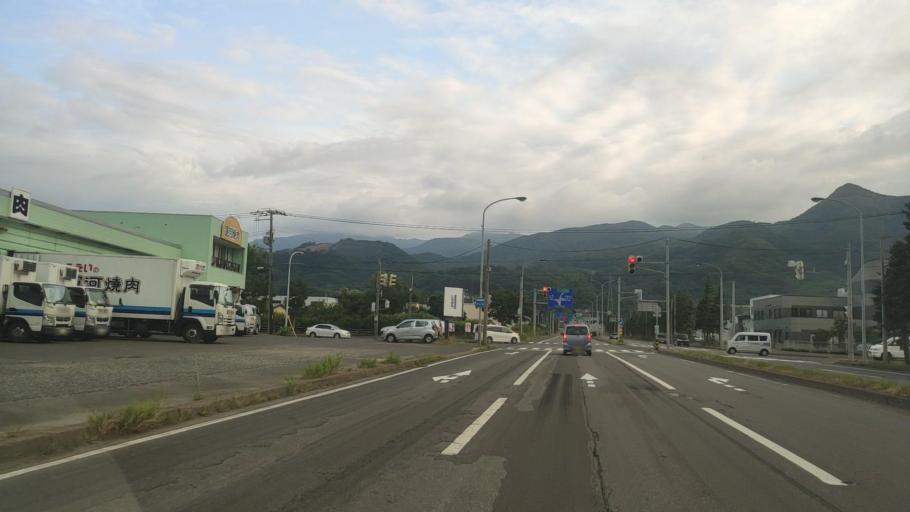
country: JP
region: Hokkaido
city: Otaru
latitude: 43.1420
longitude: 141.1794
